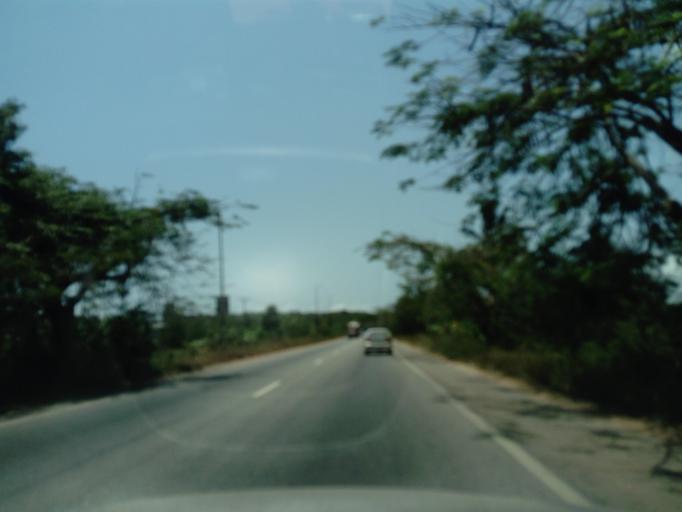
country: GH
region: Central
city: Cape Coast
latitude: 5.1196
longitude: -1.2747
